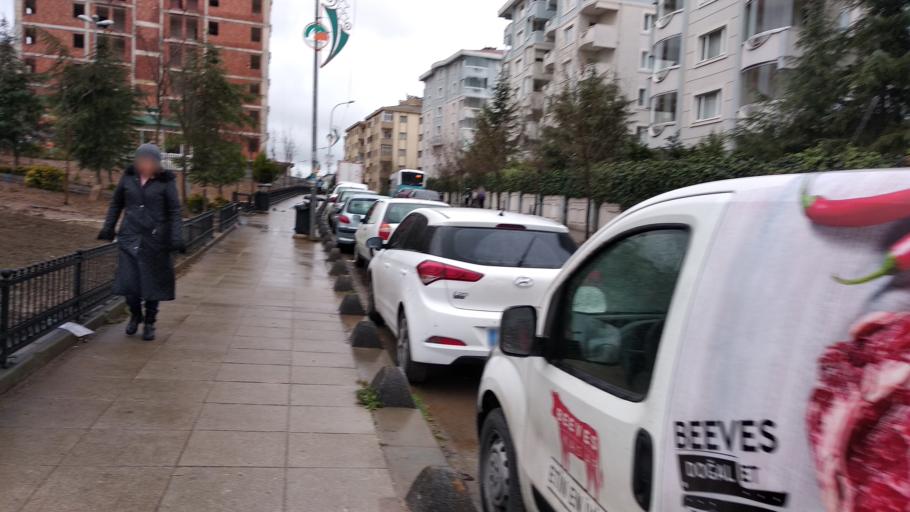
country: TR
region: Istanbul
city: Samandira
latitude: 41.0217
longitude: 29.1874
